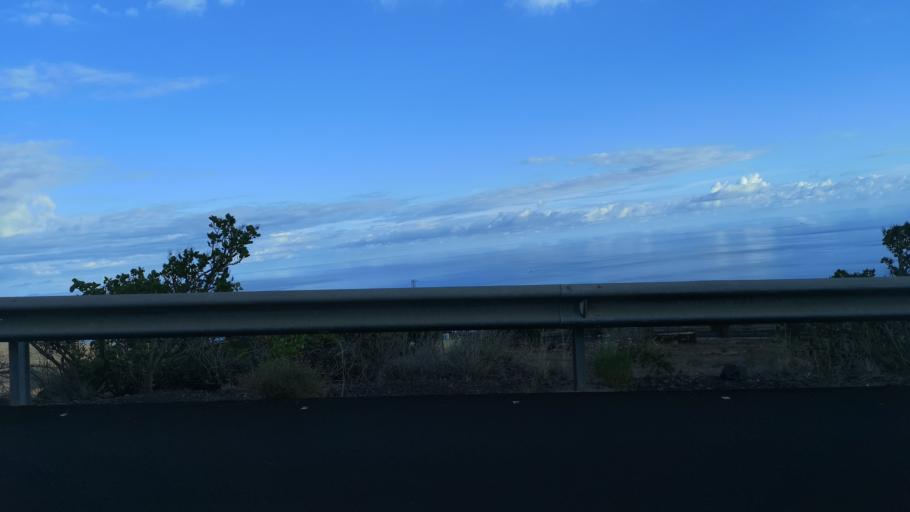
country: ES
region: Canary Islands
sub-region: Provincia de Santa Cruz de Tenerife
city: Alajero
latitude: 28.0483
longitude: -17.1973
